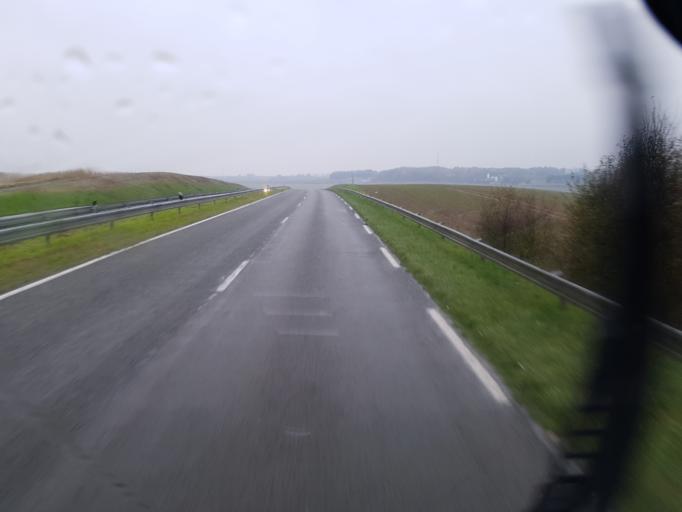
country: FR
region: Picardie
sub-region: Departement de l'Aisne
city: Essigny-le-Grand
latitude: 49.8027
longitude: 3.2858
